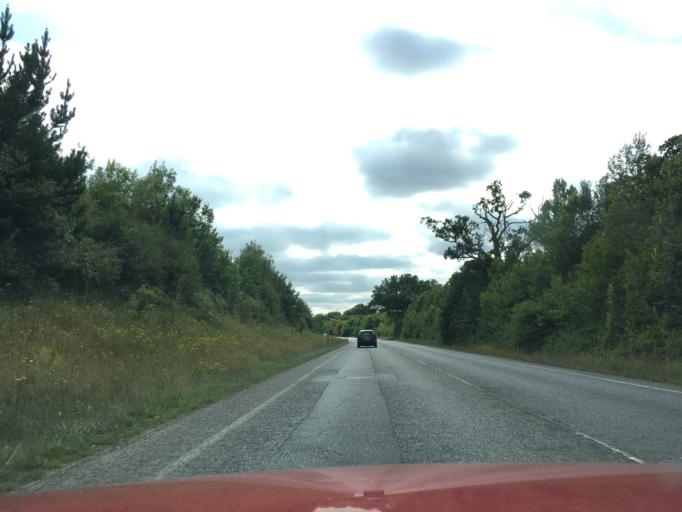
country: GB
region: England
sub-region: West Sussex
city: Billingshurst
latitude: 51.0260
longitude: -0.4557
